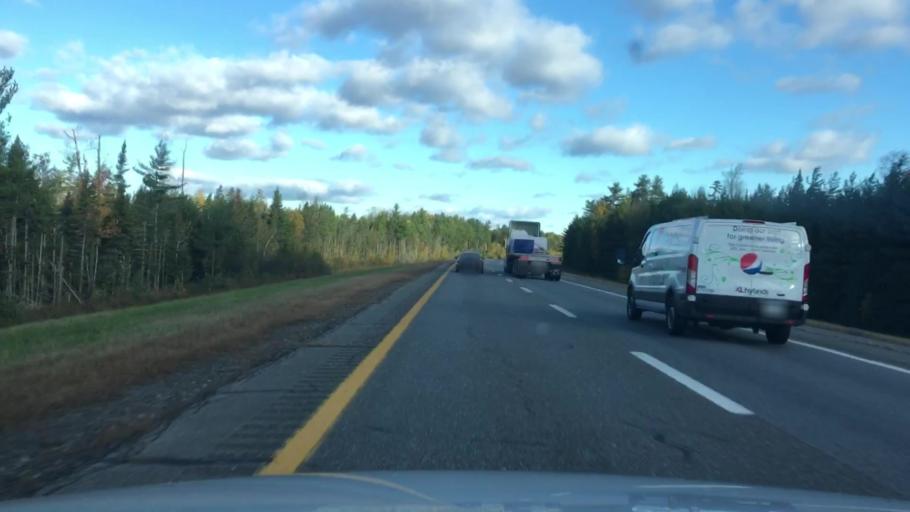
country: US
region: Maine
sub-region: Penobscot County
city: Greenbush
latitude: 45.1477
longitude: -68.7029
